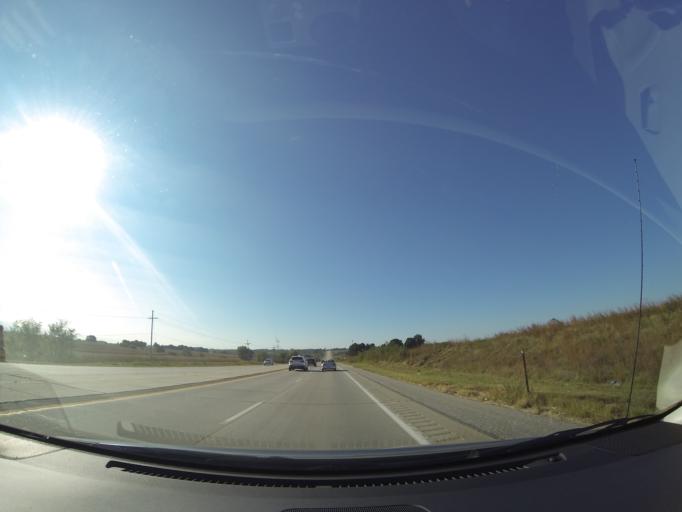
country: US
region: Nebraska
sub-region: Sarpy County
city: Gretna
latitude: 41.1836
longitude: -96.2343
